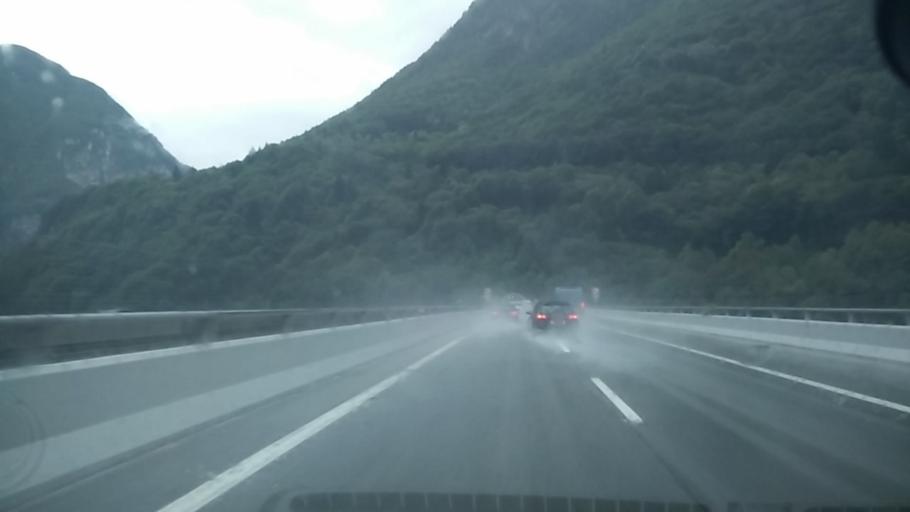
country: IT
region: Friuli Venezia Giulia
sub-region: Provincia di Udine
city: Dogna
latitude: 46.4587
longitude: 13.3038
